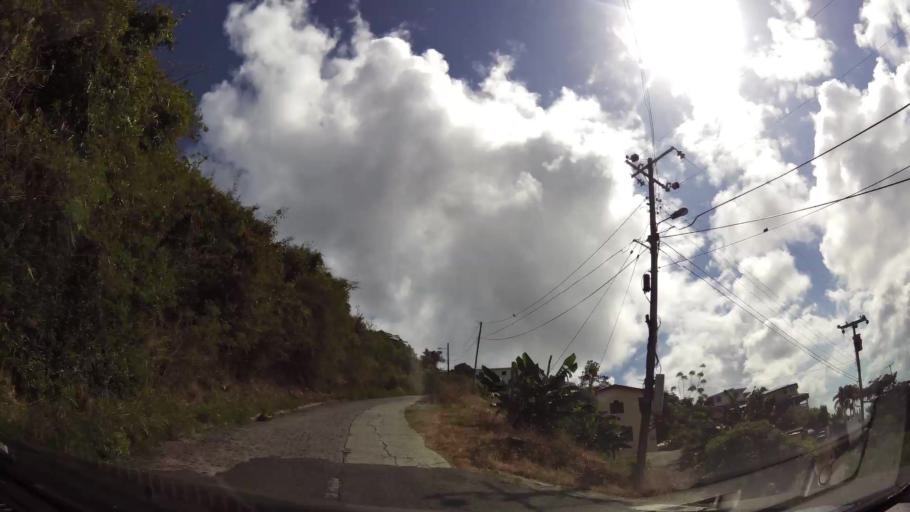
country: VG
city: Road Town
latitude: 18.4312
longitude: -64.6213
